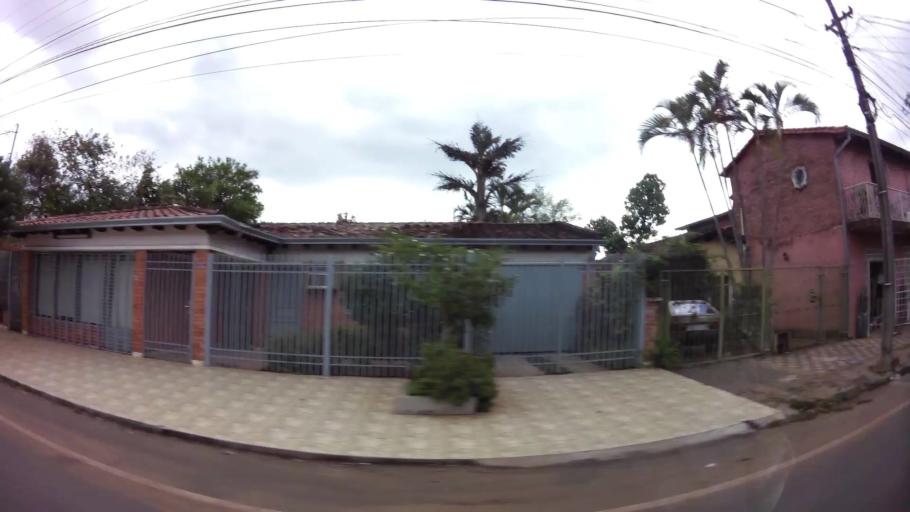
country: PY
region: Central
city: Fernando de la Mora
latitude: -25.3298
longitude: -57.5545
